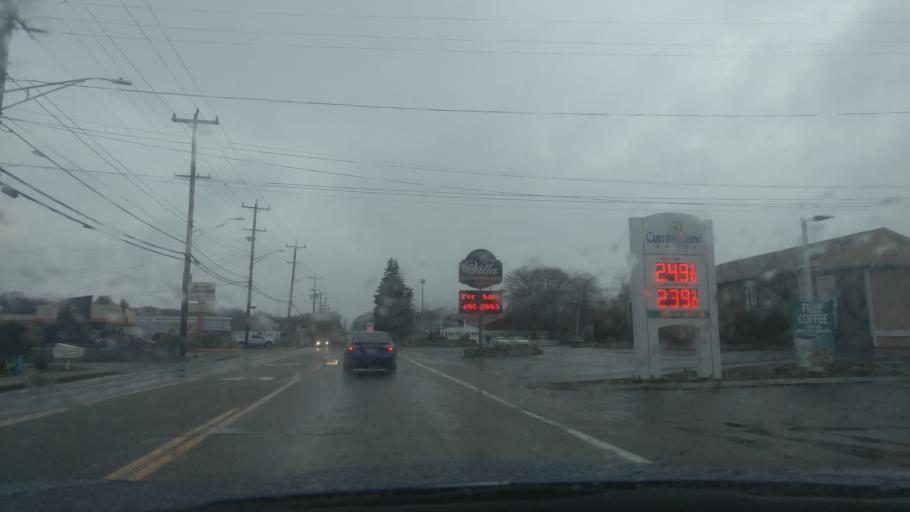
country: US
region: Rhode Island
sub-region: Kent County
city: West Warwick
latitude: 41.6850
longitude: -71.5062
